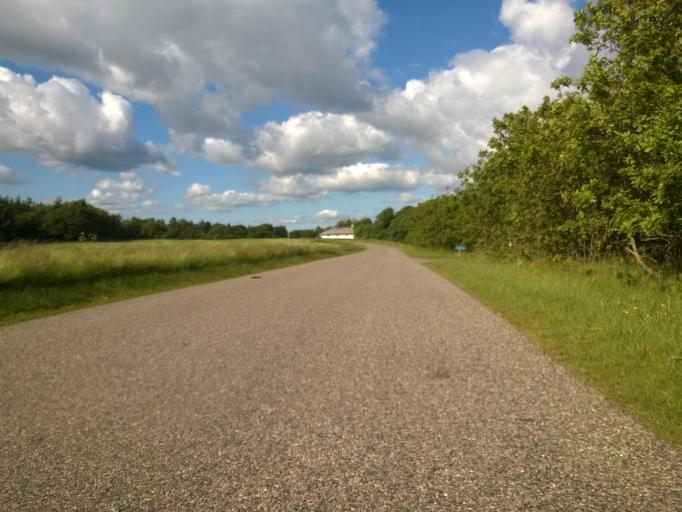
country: DK
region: Central Jutland
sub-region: Holstebro Kommune
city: Vinderup
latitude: 56.4771
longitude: 8.8621
